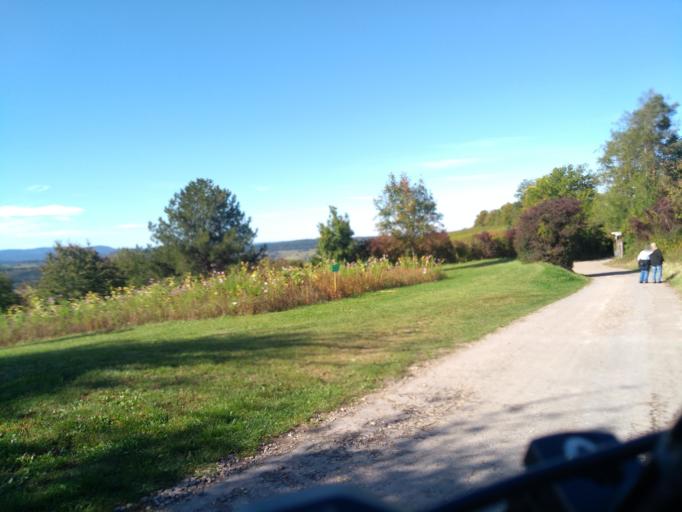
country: DE
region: Baden-Wuerttemberg
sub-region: Karlsruhe Region
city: Birkenfeld
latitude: 48.9030
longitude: 8.6022
